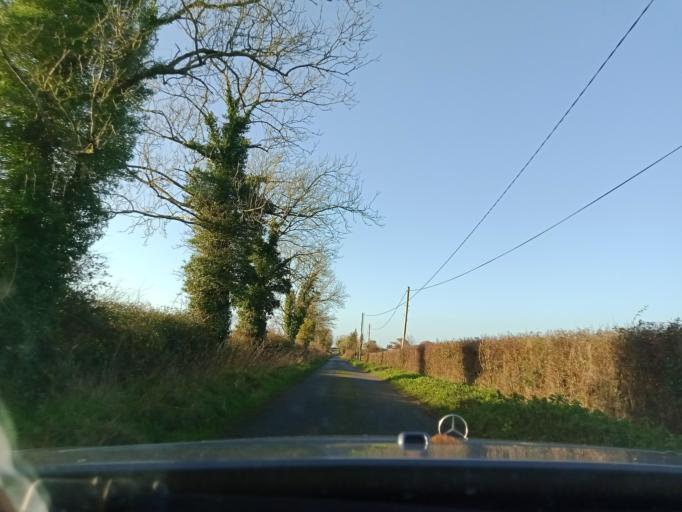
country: IE
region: Leinster
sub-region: Kilkenny
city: Callan
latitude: 52.5021
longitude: -7.4233
